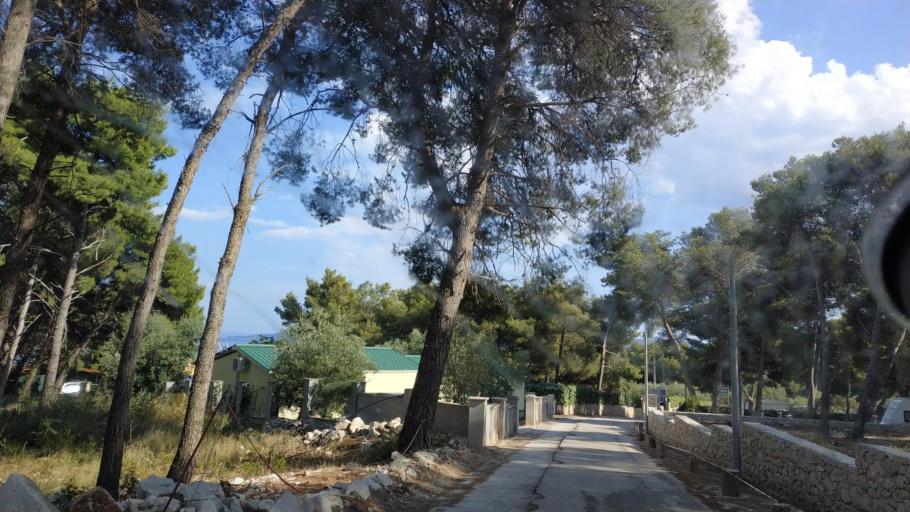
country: HR
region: Splitsko-Dalmatinska
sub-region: Grad Trogir
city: Trogir
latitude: 43.4828
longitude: 16.2445
